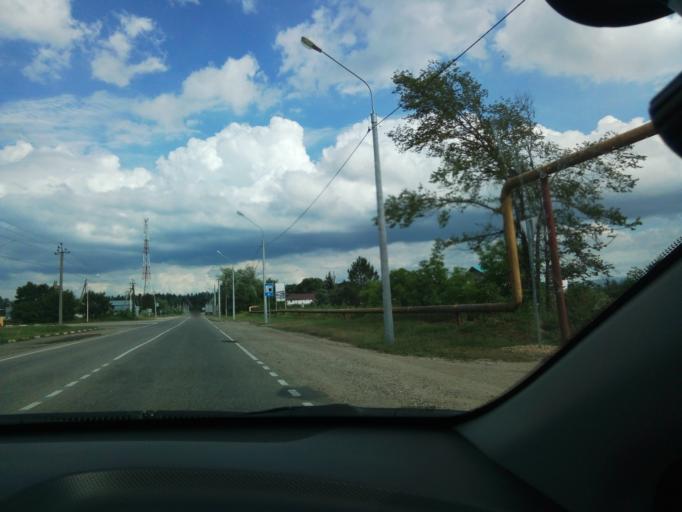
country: RU
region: Krasnodarskiy
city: Apsheronsk
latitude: 44.4385
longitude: 39.7571
